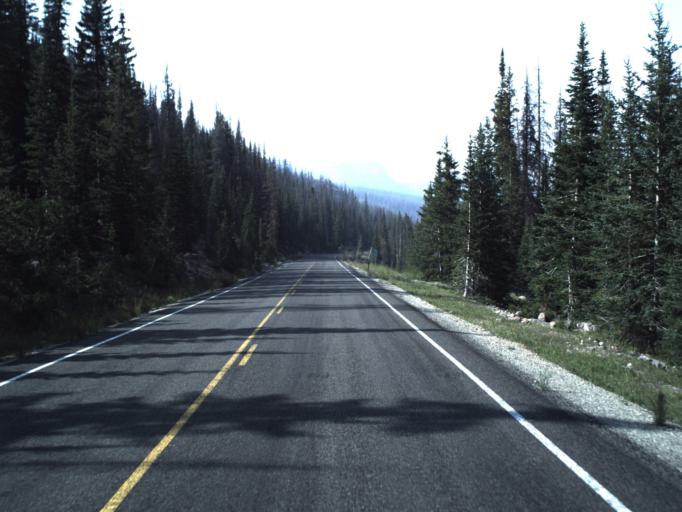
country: US
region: Utah
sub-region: Summit County
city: Kamas
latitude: 40.7456
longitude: -110.8730
